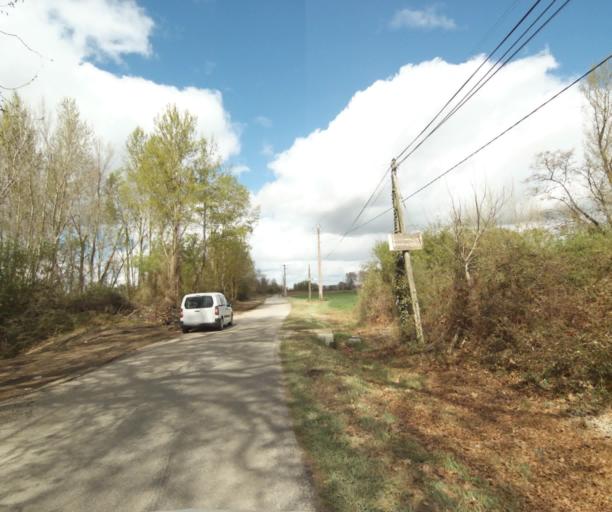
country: FR
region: Midi-Pyrenees
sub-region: Departement de l'Ariege
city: Saverdun
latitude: 43.2500
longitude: 1.5820
